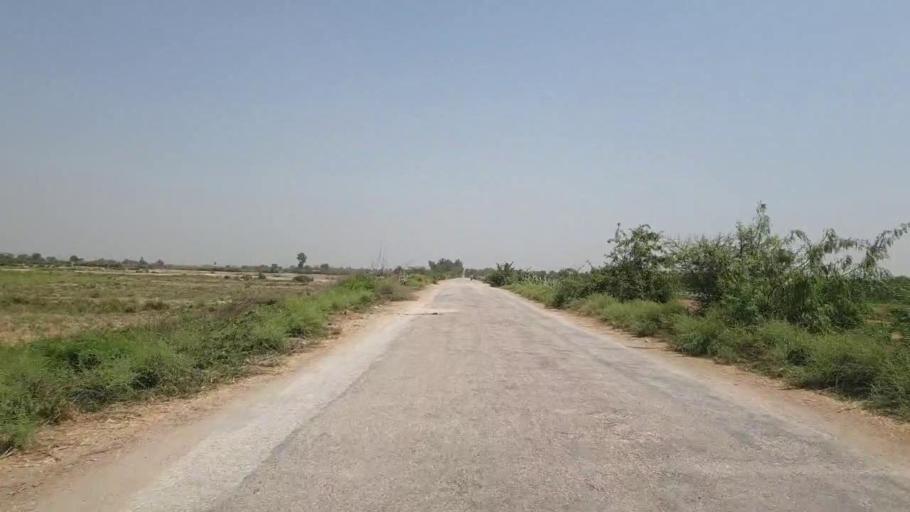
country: PK
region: Sindh
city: Adilpur
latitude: 27.9047
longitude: 69.2959
